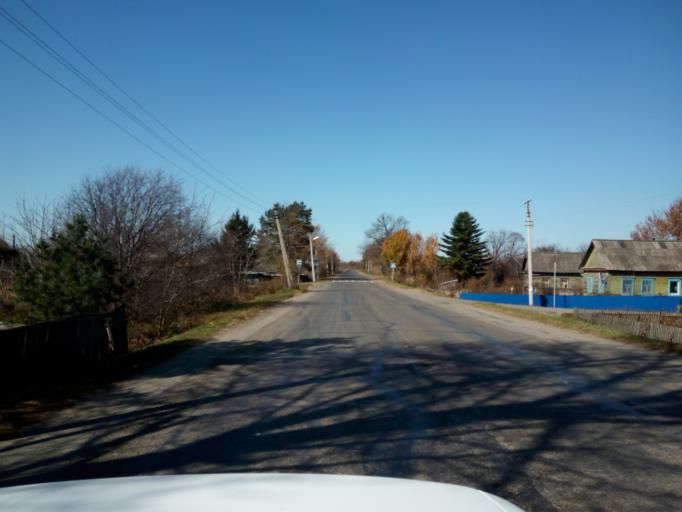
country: RU
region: Primorskiy
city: Dal'nerechensk
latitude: 45.9153
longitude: 133.7870
